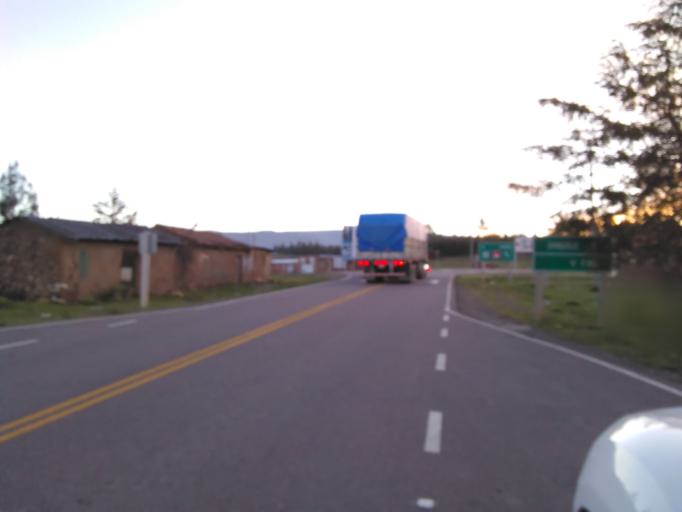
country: BO
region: Cochabamba
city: Arani
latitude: -17.5473
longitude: -65.6731
